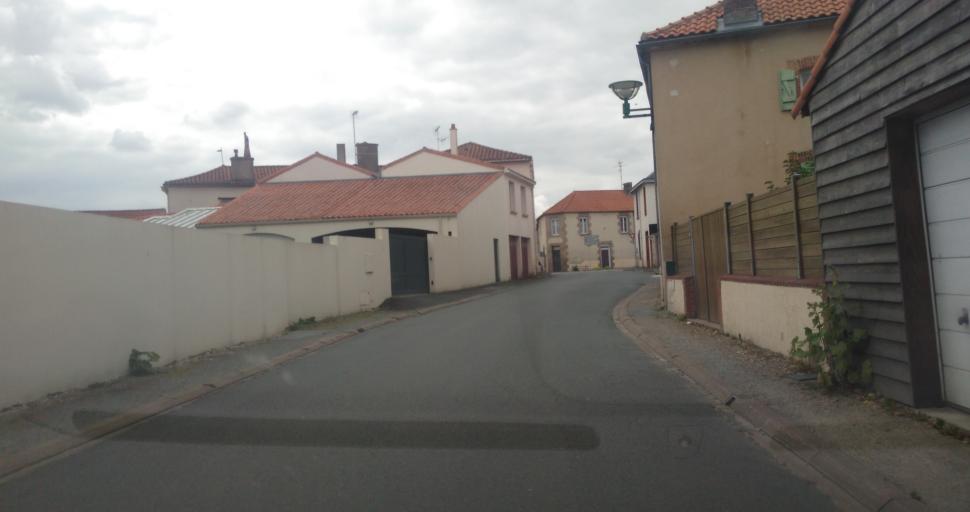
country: FR
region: Pays de la Loire
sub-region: Departement de la Vendee
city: La Chaize-le-Vicomte
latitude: 46.6735
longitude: -1.2952
